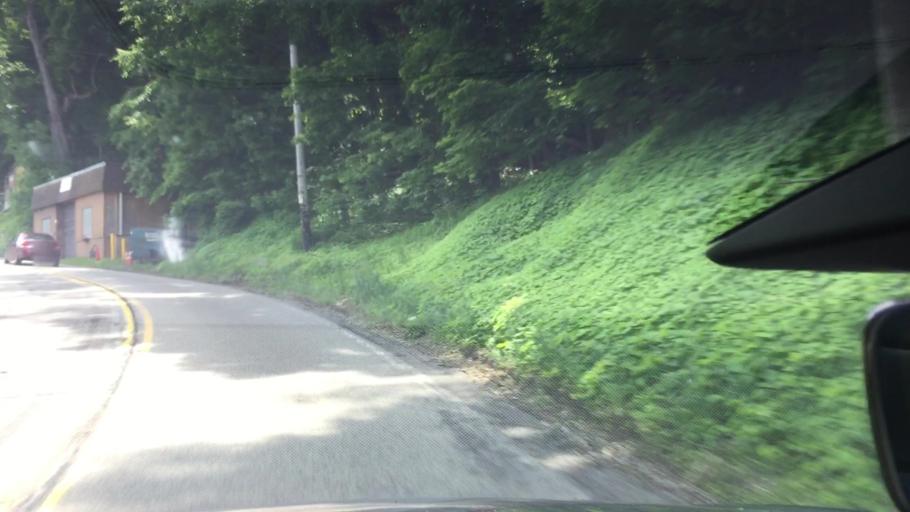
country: US
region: Pennsylvania
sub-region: Allegheny County
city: Blawnox
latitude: 40.4776
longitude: -79.8438
